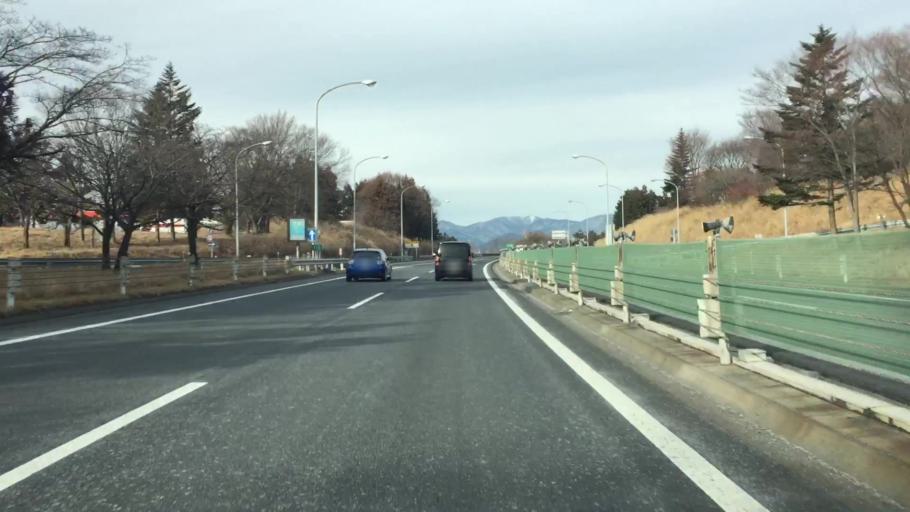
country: JP
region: Gunma
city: Numata
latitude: 36.6012
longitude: 139.0629
